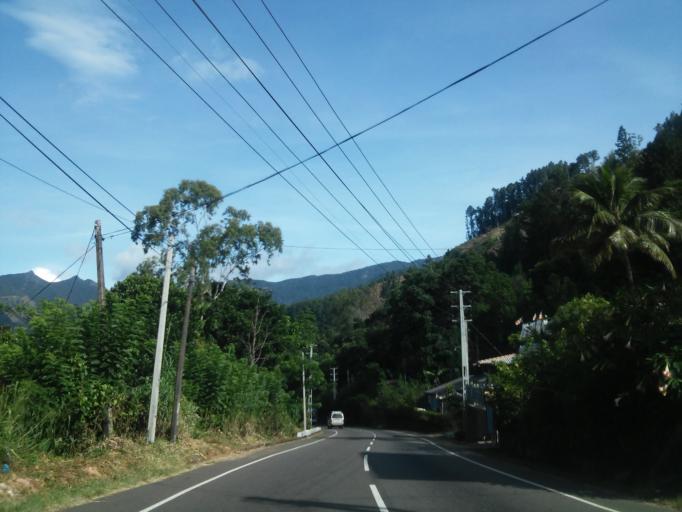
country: LK
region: Uva
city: Haputale
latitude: 6.7637
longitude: 80.8728
